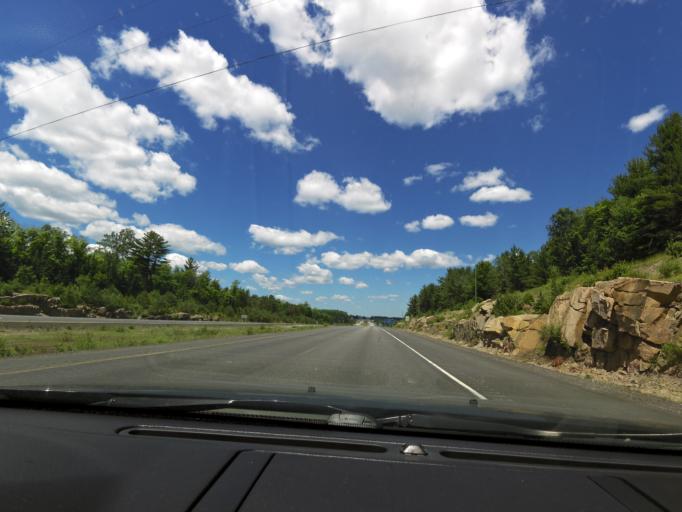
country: CA
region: Ontario
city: Huntsville
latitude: 45.4961
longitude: -79.2924
